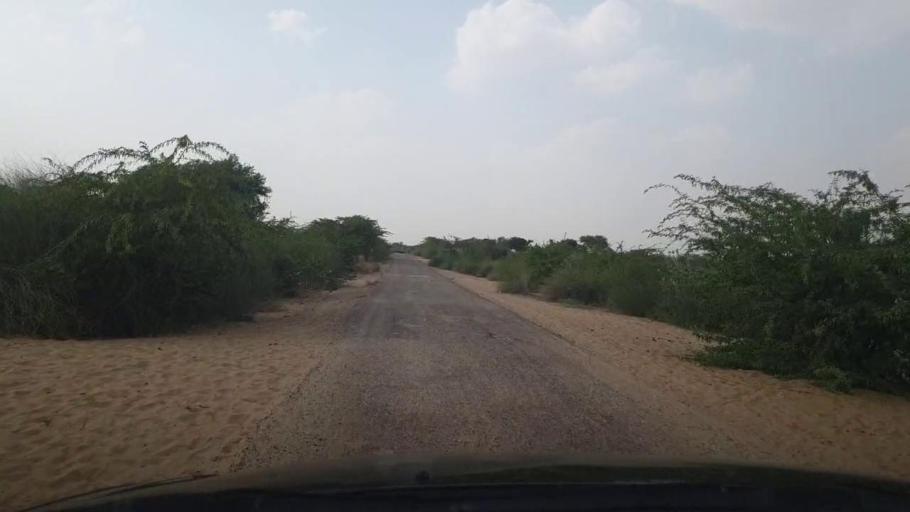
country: PK
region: Sindh
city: Islamkot
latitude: 24.9838
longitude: 70.5799
